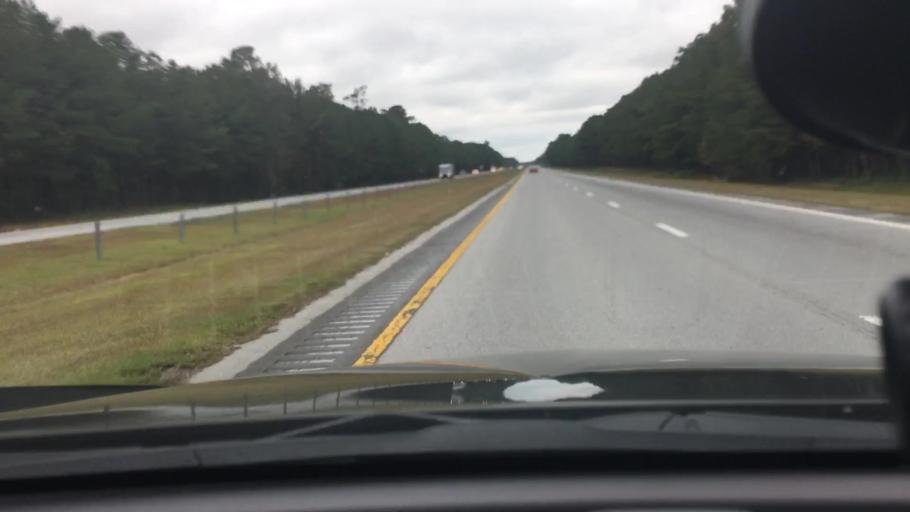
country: US
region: North Carolina
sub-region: Pitt County
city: Farmville
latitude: 35.6312
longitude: -77.7181
